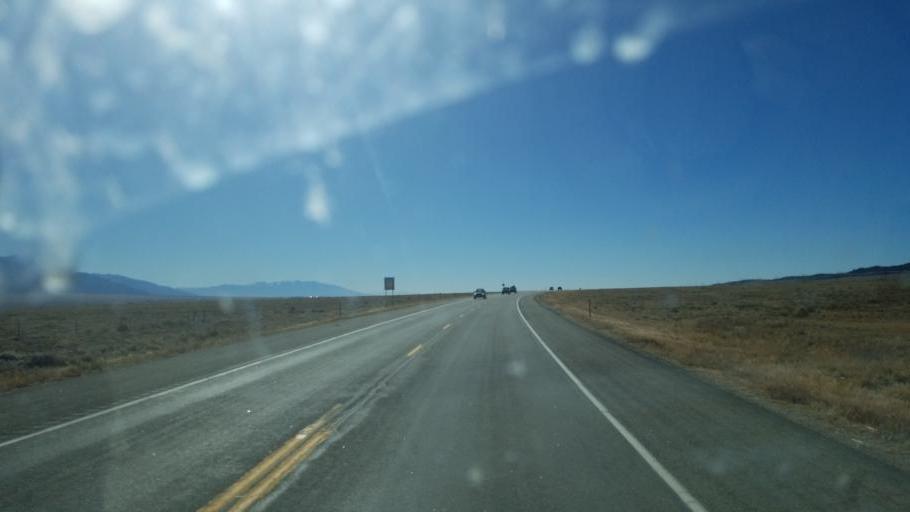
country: US
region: Colorado
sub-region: Saguache County
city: Saguache
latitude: 38.2433
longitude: -105.9462
